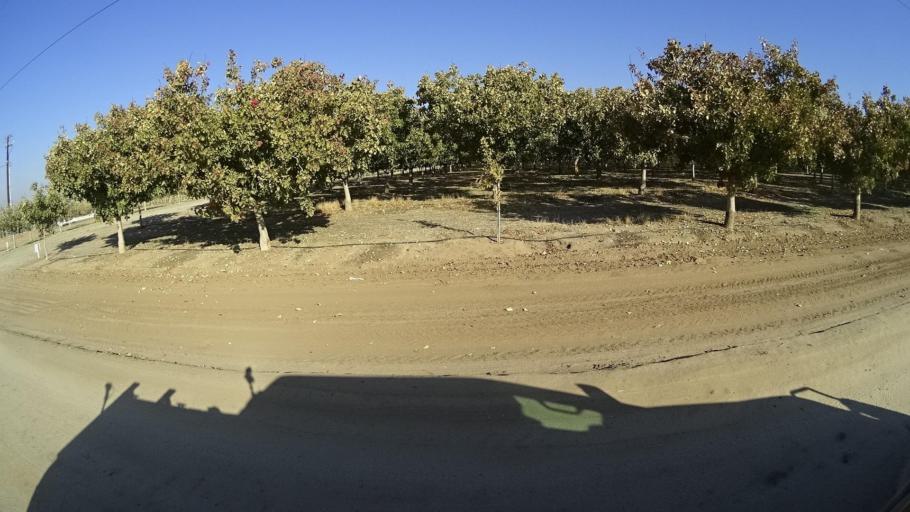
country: US
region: California
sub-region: Tulare County
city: Richgrove
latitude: 35.7328
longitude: -119.1049
